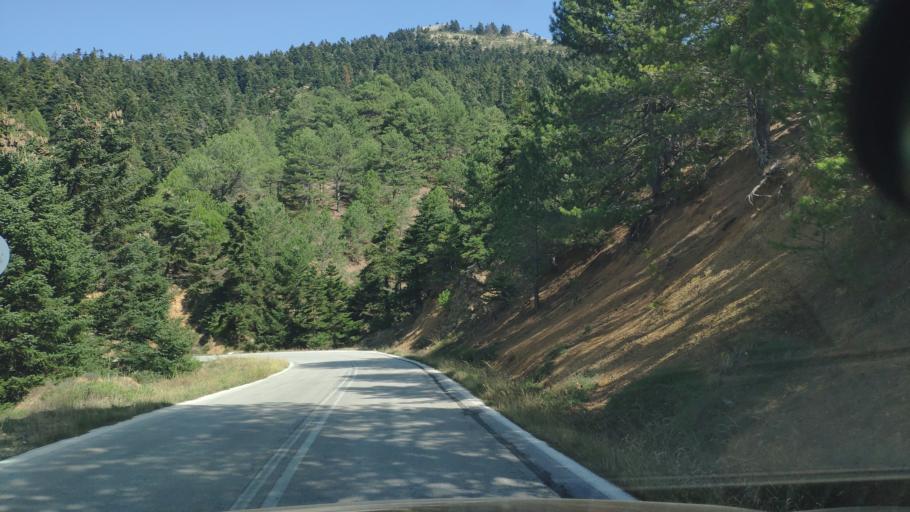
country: GR
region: West Greece
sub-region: Nomos Achaias
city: Aiyira
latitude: 37.8676
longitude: 22.3650
